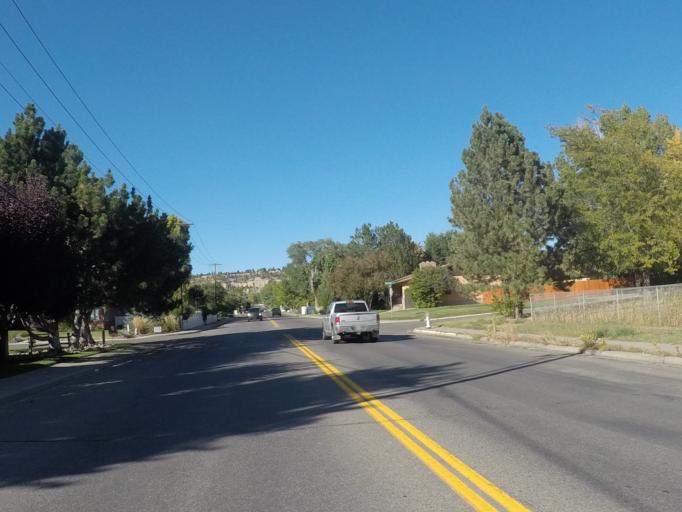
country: US
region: Montana
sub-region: Yellowstone County
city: Billings
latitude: 45.7895
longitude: -108.5904
